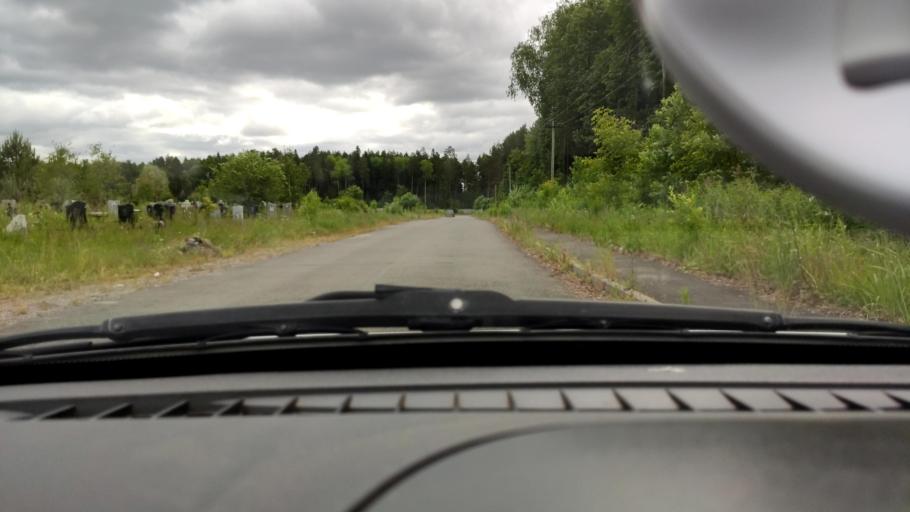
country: RU
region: Perm
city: Kondratovo
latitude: 58.0615
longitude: 56.1563
